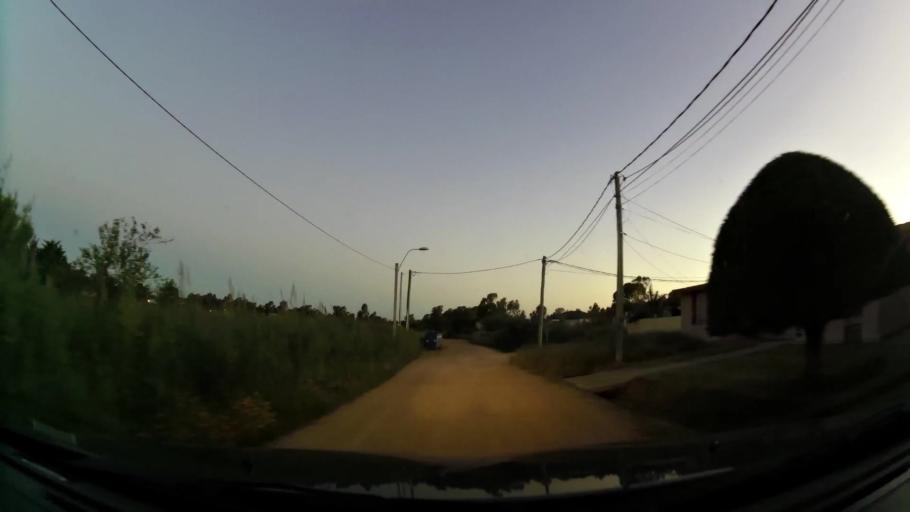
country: UY
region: Canelones
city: Colonia Nicolich
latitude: -34.8128
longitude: -55.9616
